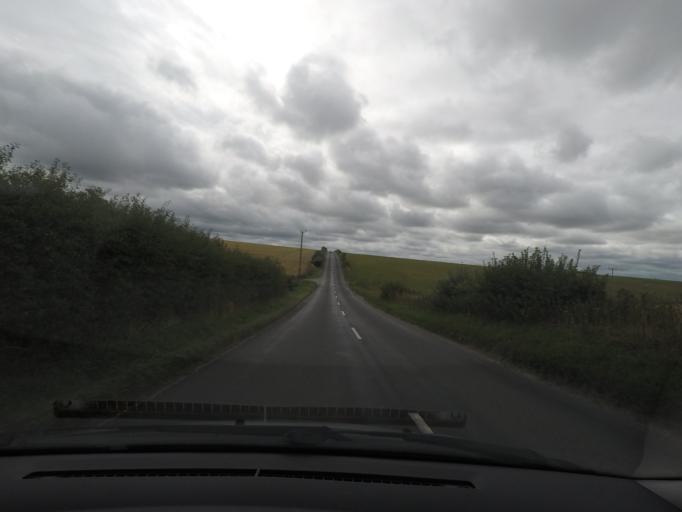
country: GB
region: England
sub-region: Wiltshire
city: Shrewton
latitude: 51.1929
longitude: -1.8616
